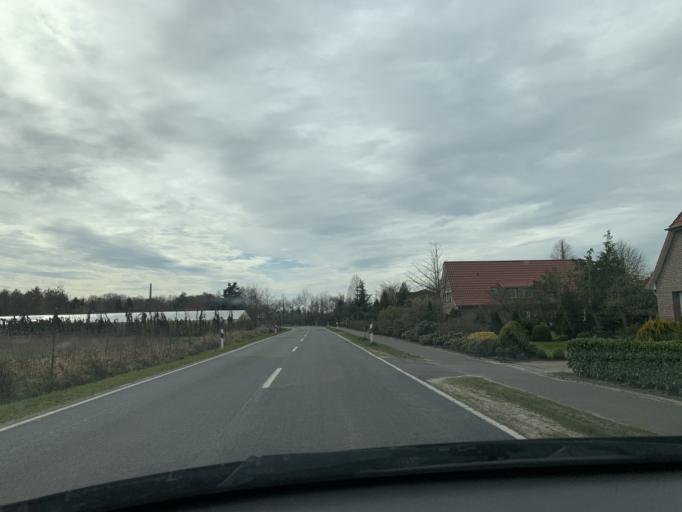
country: DE
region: Lower Saxony
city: Edewecht
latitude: 53.1546
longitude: 7.9713
